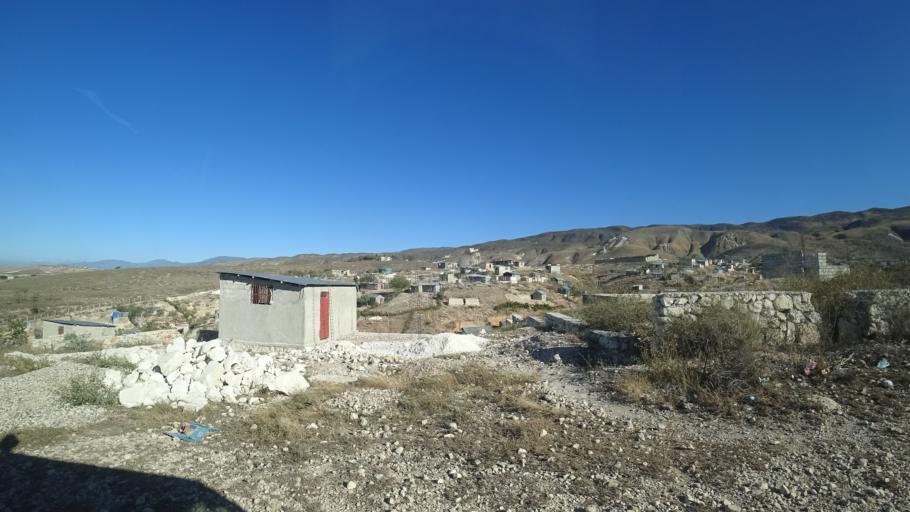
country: HT
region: Ouest
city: Cabaret
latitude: 18.6868
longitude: -72.3239
